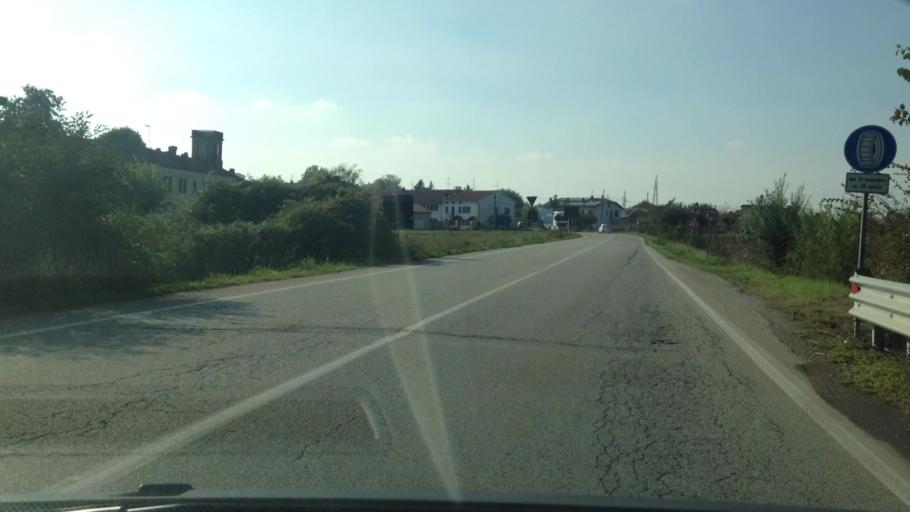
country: IT
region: Piedmont
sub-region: Provincia di Alessandria
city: Felizzano
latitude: 44.9009
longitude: 8.4381
